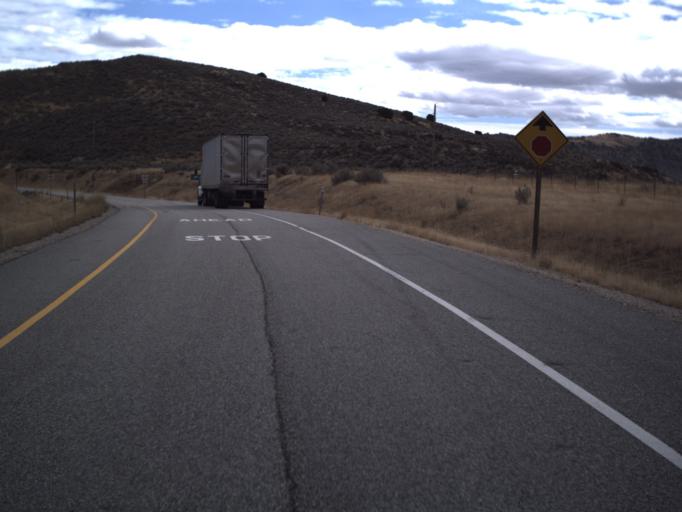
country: US
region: Idaho
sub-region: Oneida County
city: Malad City
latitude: 41.8966
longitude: -112.5767
